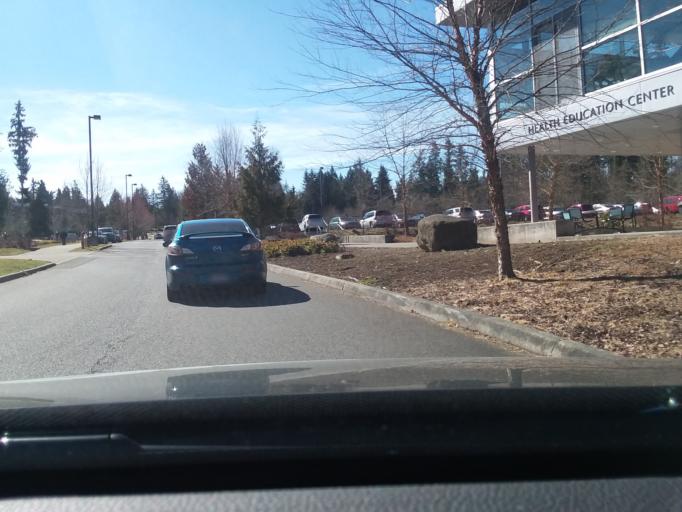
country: US
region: Washington
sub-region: Pierce County
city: South Hill
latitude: 47.1594
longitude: -122.2739
